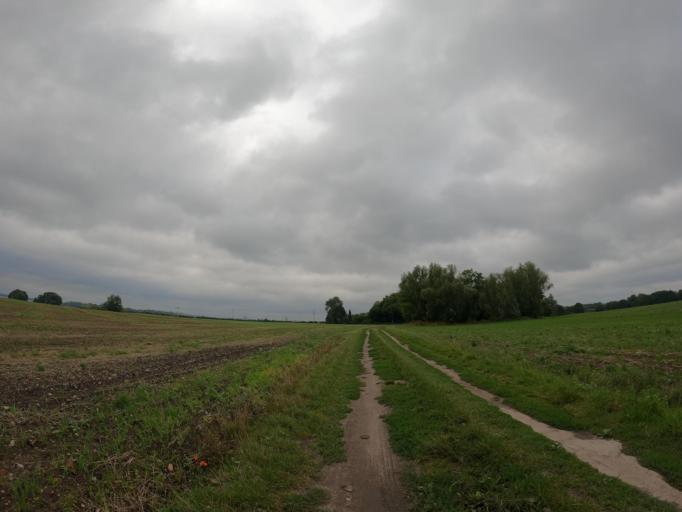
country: DE
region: Mecklenburg-Vorpommern
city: Altefahr
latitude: 54.3206
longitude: 13.1497
